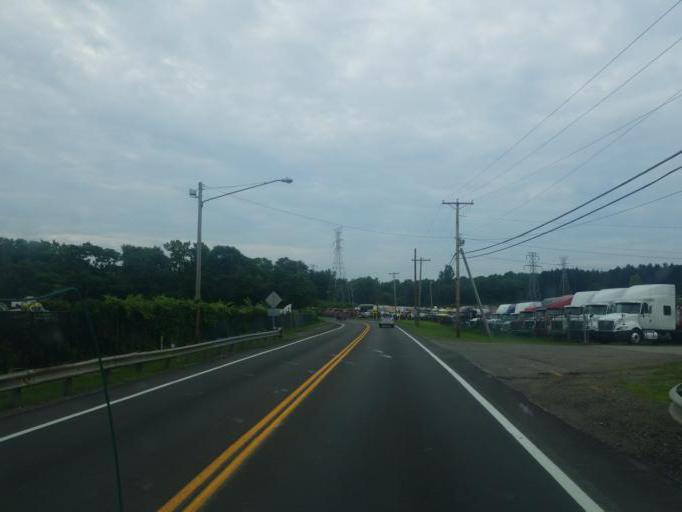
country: US
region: Ohio
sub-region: Stark County
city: Canton
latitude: 40.7752
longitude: -81.3467
